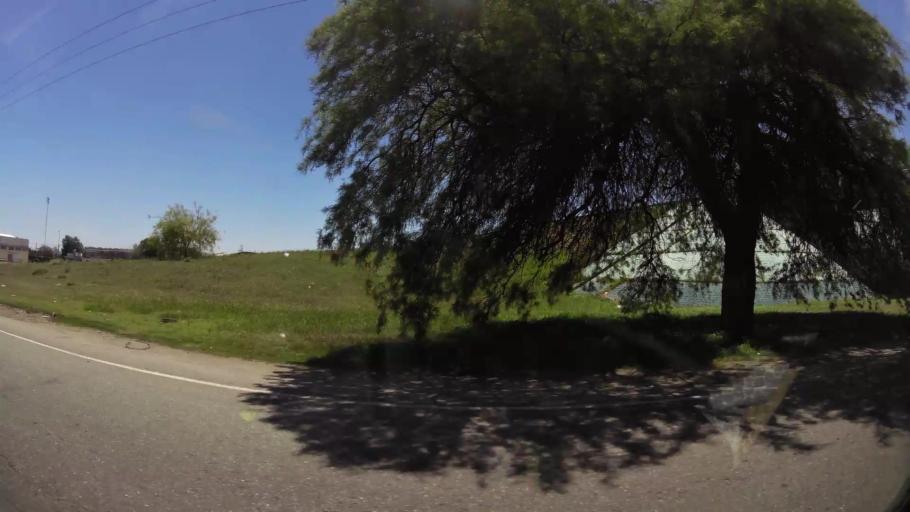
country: AR
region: Cordoba
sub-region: Departamento de Capital
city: Cordoba
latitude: -31.4435
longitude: -64.1250
